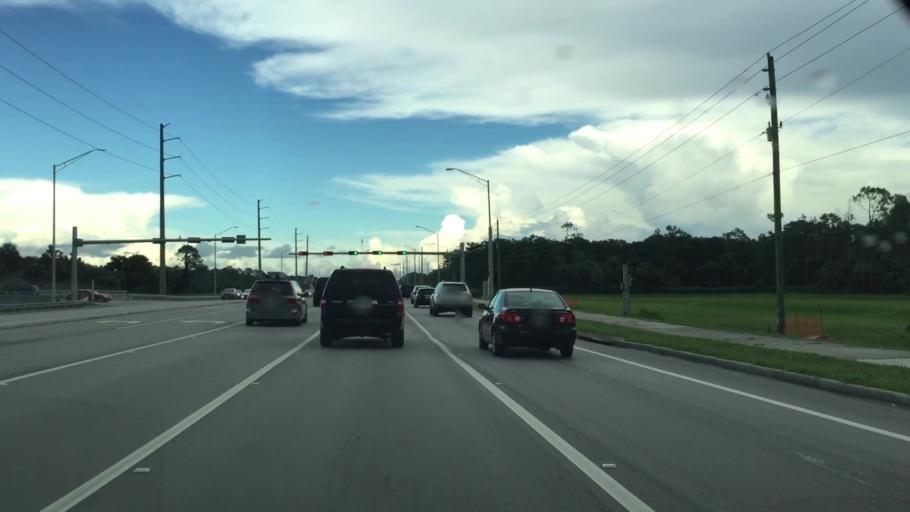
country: US
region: Florida
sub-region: Collier County
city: Orangetree
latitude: 26.2752
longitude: -81.6249
